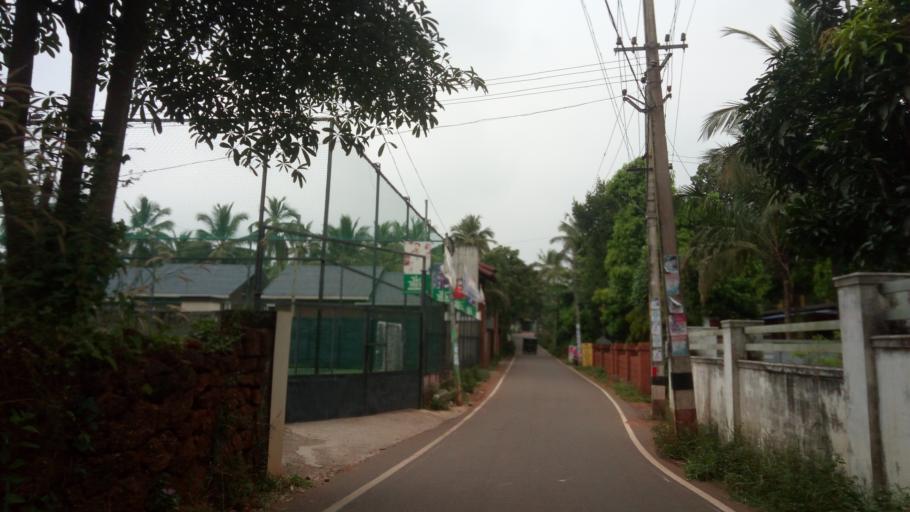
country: IN
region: Kerala
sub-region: Malappuram
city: Malappuram
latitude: 10.9807
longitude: 76.0064
